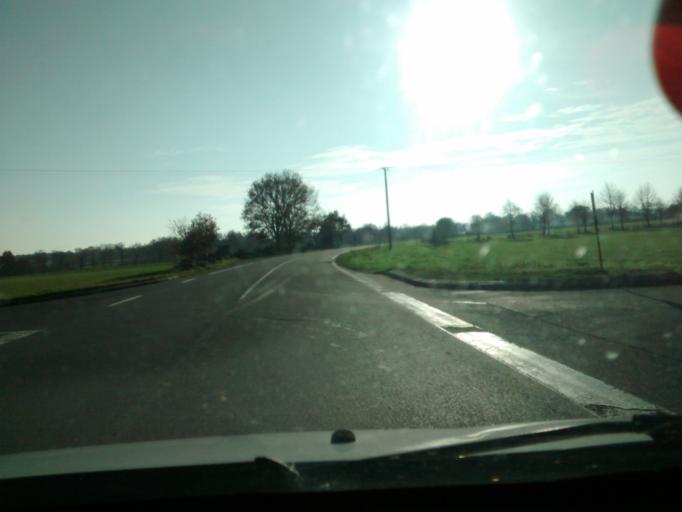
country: FR
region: Brittany
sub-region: Departement d'Ille-et-Vilaine
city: Tremblay
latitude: 48.3917
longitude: -1.4871
